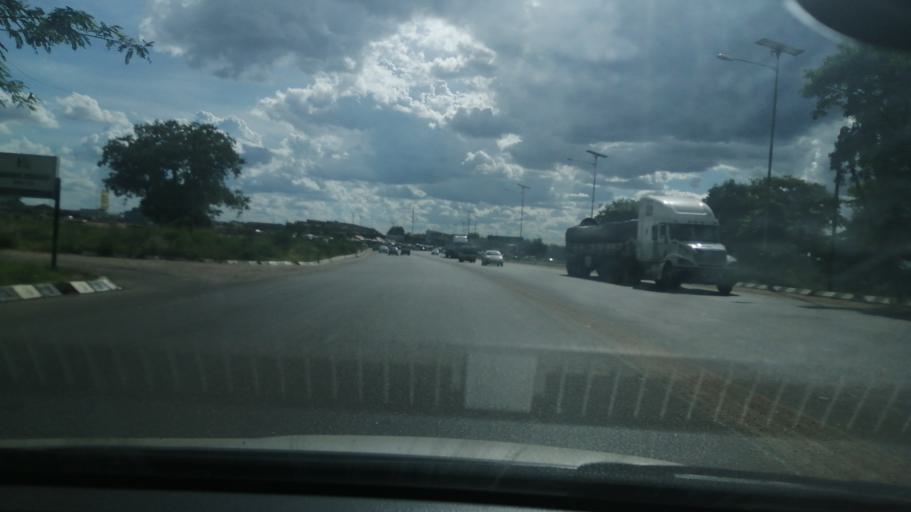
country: ZW
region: Harare
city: Harare
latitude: -17.8508
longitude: 31.0571
